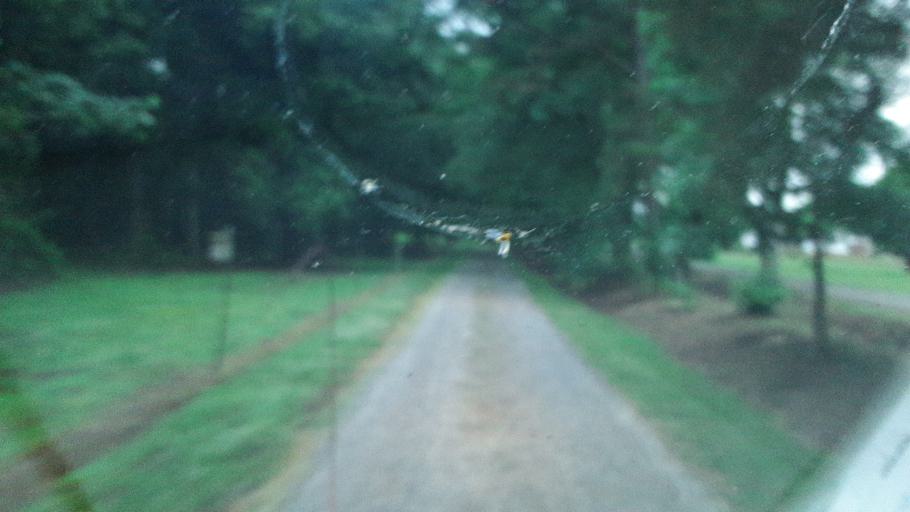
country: US
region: North Carolina
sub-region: Yadkin County
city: Jonesville
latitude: 36.1164
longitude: -80.8582
